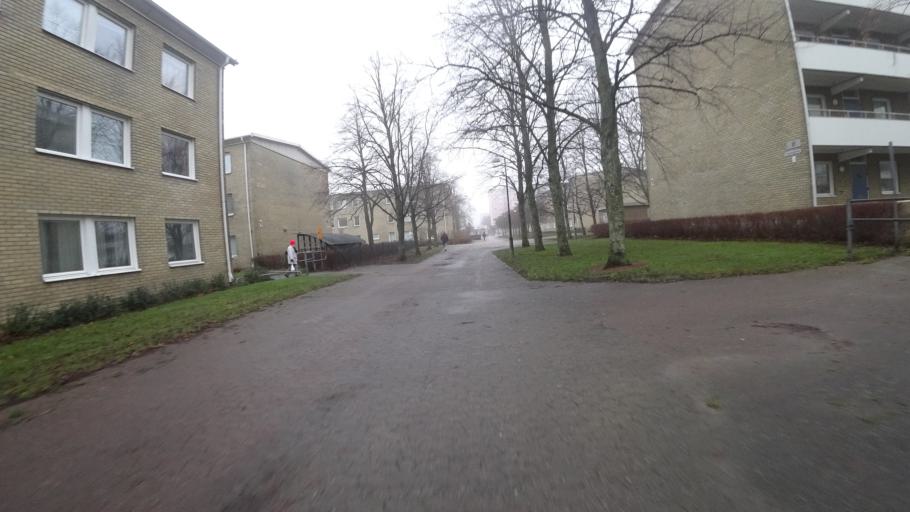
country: SE
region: Skane
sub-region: Malmo
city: Malmoe
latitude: 55.5750
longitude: 12.9865
